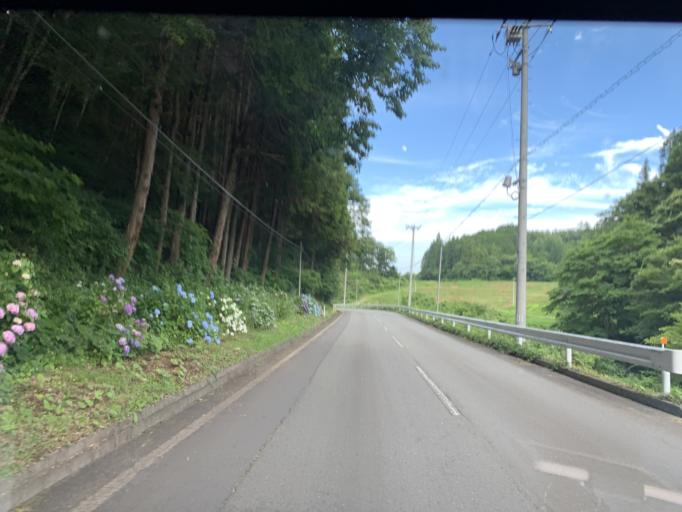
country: JP
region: Iwate
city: Ichinoseki
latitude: 38.8997
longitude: 140.9994
